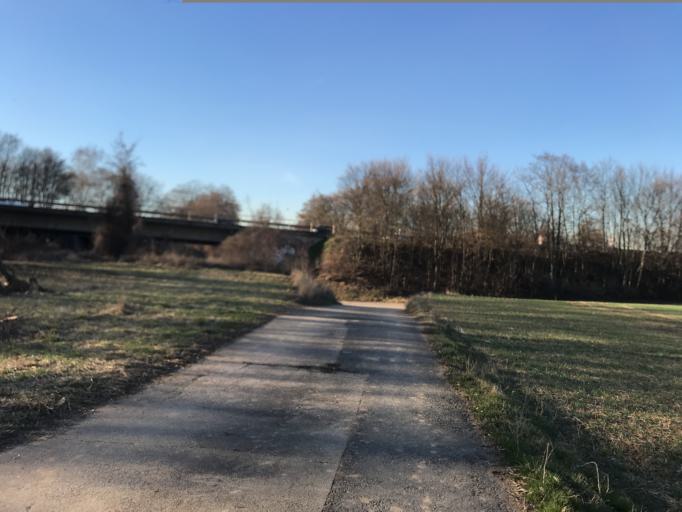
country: DE
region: Rheinland-Pfalz
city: Klein-Winternheim
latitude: 49.9546
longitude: 8.2295
